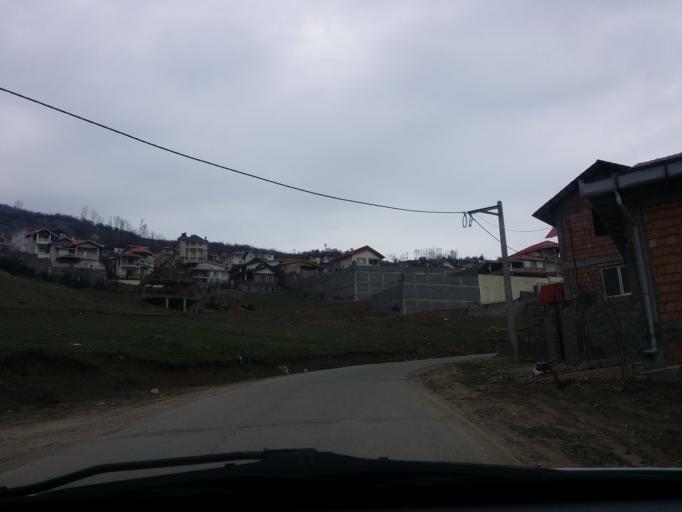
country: IR
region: Mazandaran
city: `Abbasabad
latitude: 36.5286
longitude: 51.1599
